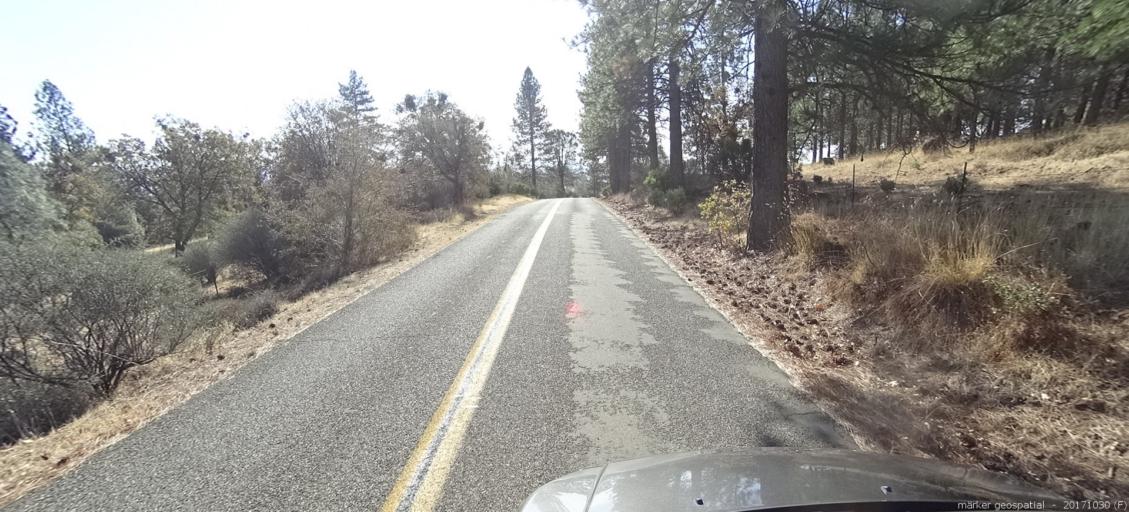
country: US
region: California
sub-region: Shasta County
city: Shingletown
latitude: 40.6804
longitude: -121.9467
